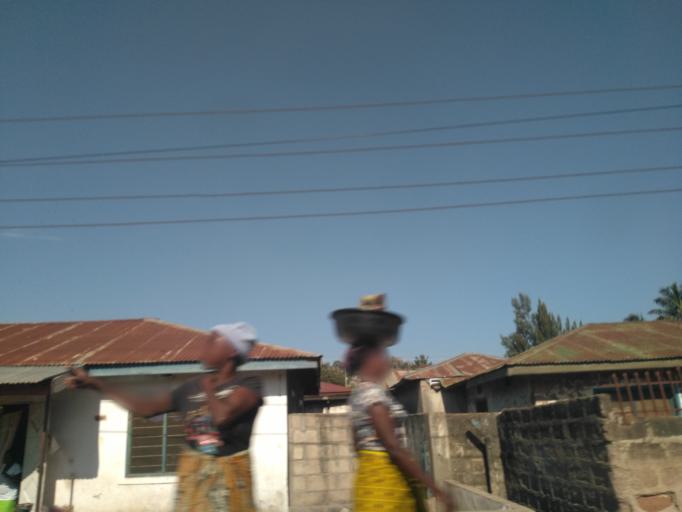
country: TZ
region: Mwanza
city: Mwanza
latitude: -2.5045
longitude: 32.8964
